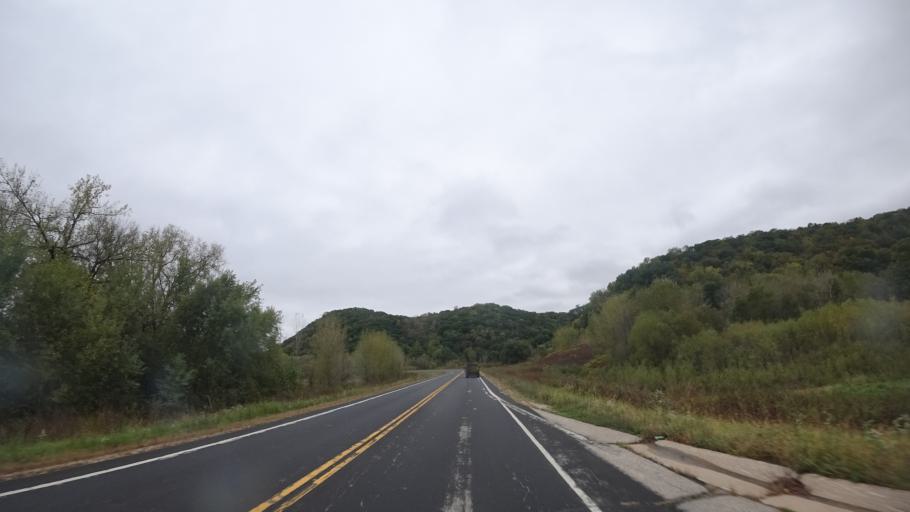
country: US
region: Wisconsin
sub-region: Grant County
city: Boscobel
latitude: 43.1459
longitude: -90.7299
